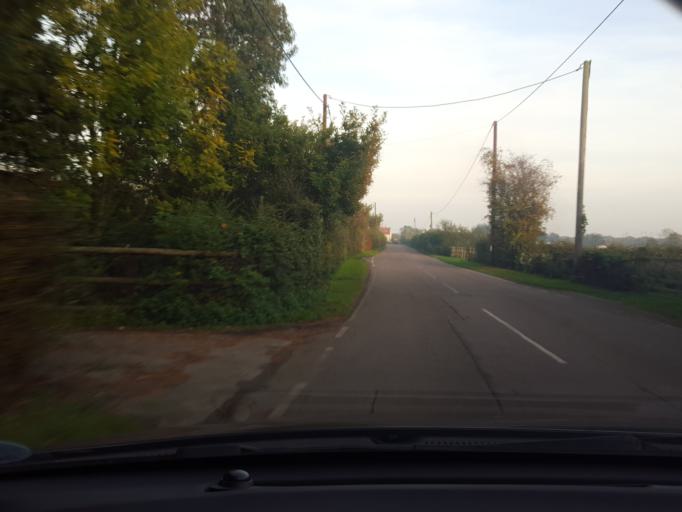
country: GB
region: England
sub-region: Essex
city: Saint Osyth
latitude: 51.8224
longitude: 1.1059
